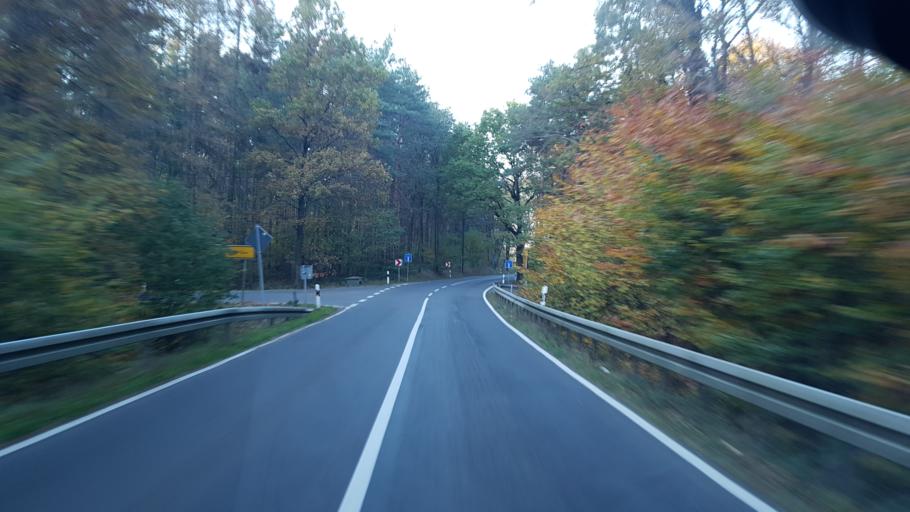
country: DE
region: Saxony
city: Schildau
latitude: 51.4244
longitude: 12.9709
